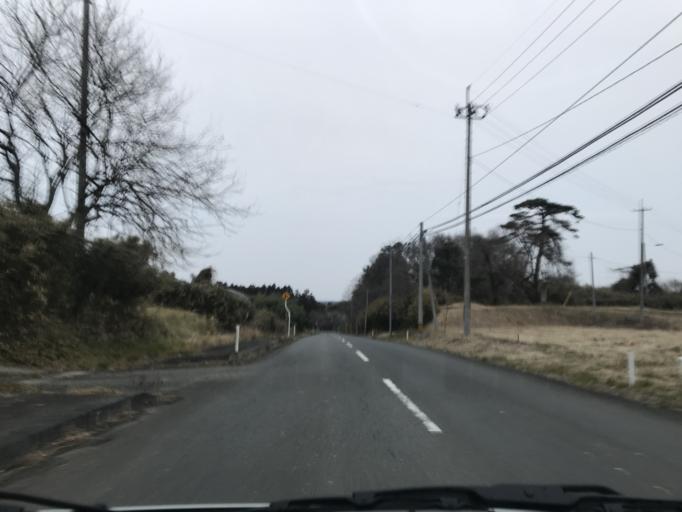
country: JP
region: Miyagi
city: Kogota
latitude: 38.6974
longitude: 141.0956
